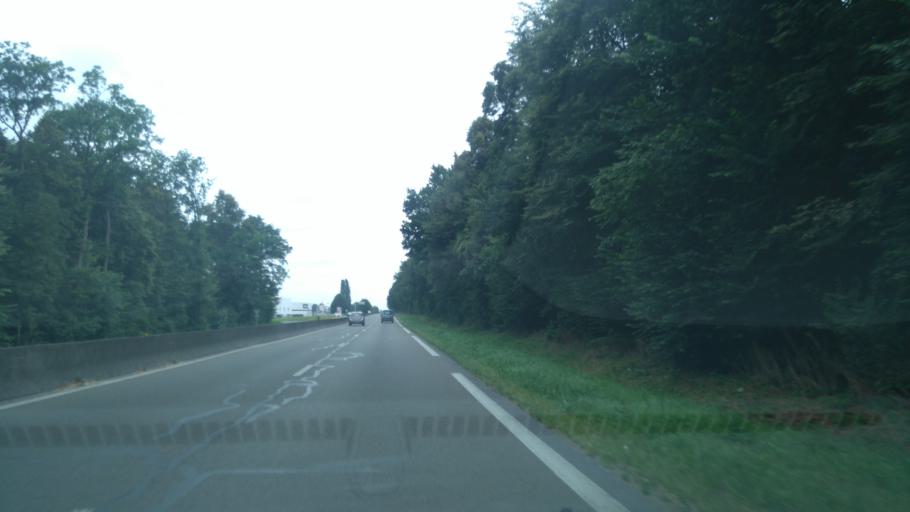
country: FR
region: Picardie
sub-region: Departement de l'Oise
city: Saint-Maximin
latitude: 49.2268
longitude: 2.4691
